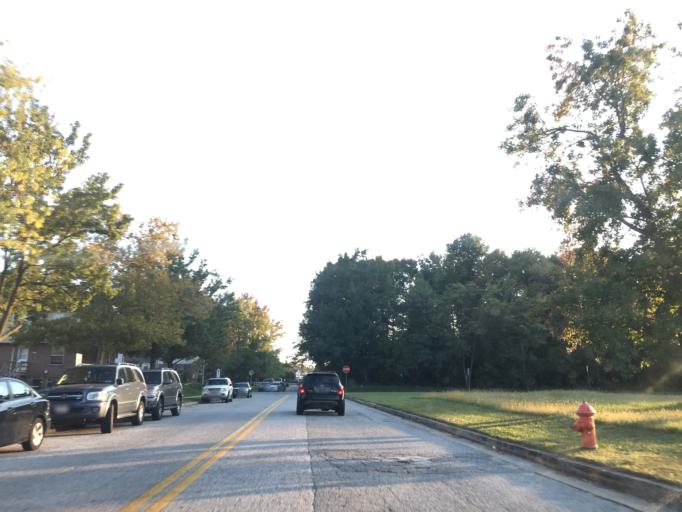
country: US
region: Maryland
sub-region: Baltimore County
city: Essex
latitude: 39.2942
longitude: -76.4474
